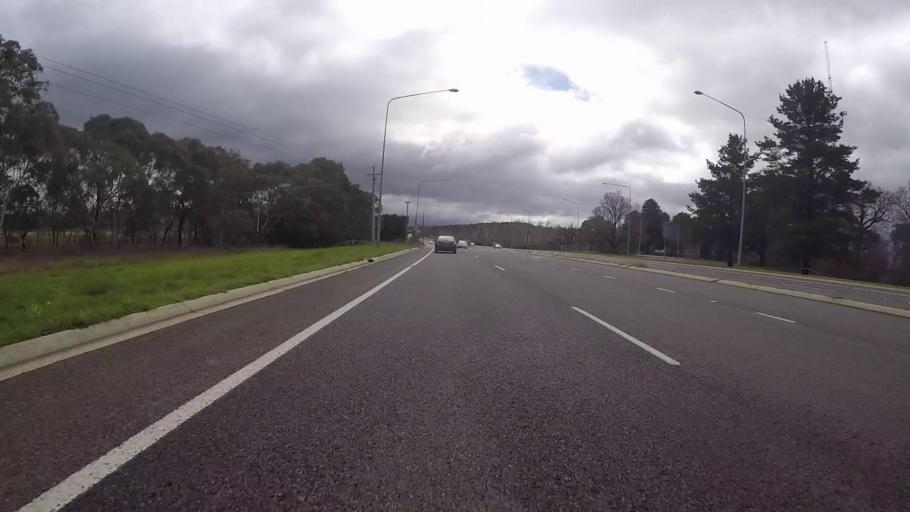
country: AU
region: Australian Capital Territory
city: Kaleen
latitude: -35.2203
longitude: 149.1194
